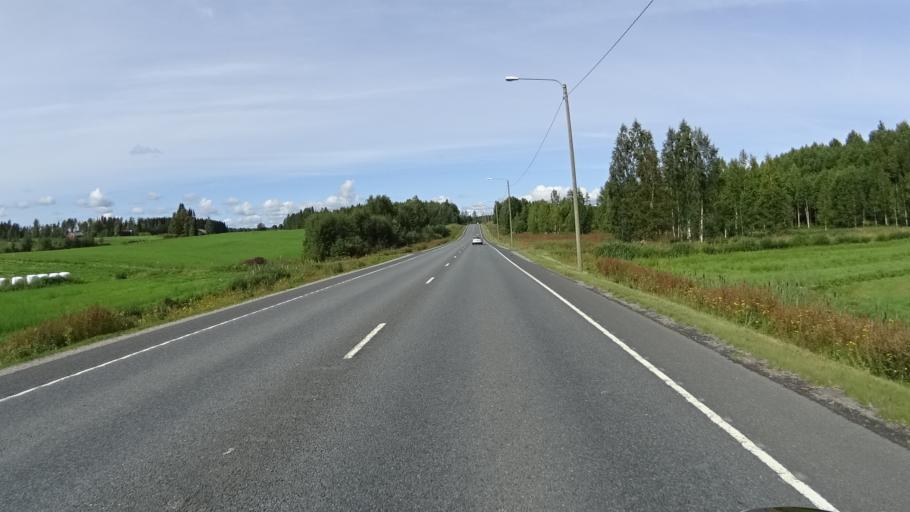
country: FI
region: Pirkanmaa
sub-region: Tampere
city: Haemeenkyroe
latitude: 61.6574
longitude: 23.1706
